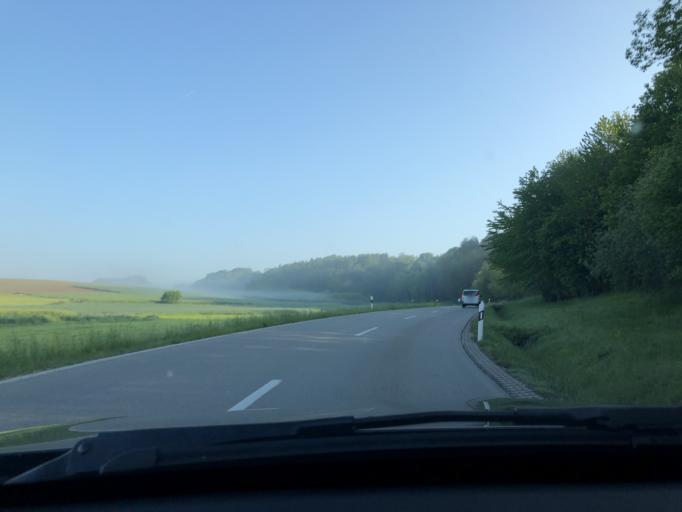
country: DE
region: Bavaria
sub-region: Upper Bavaria
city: Kirchdorf
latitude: 48.4627
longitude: 11.6479
